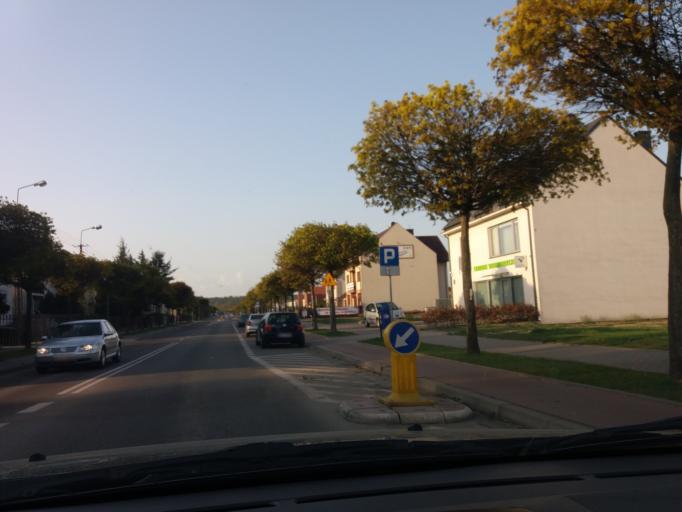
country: PL
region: Masovian Voivodeship
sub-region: Powiat mlawski
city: Mlawa
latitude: 53.1175
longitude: 20.3759
